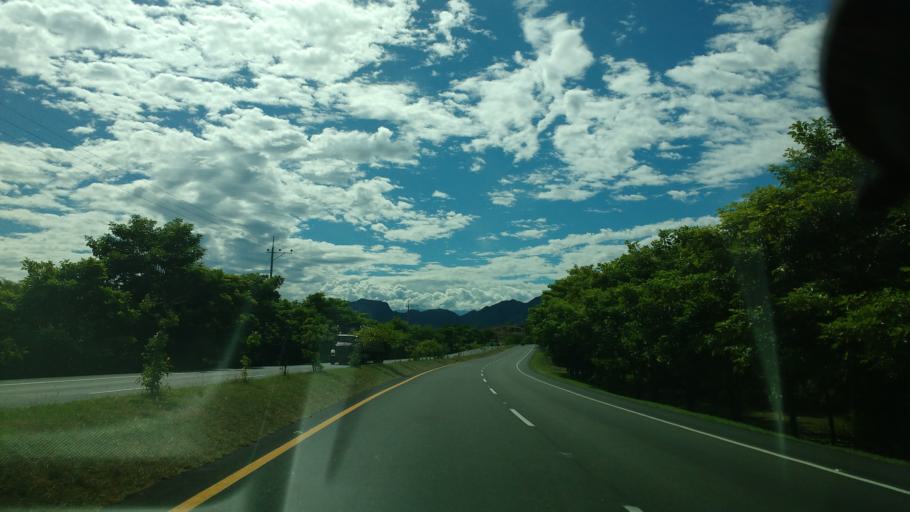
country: CO
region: Tolima
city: Valle de San Juan
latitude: 4.2517
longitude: -74.9860
